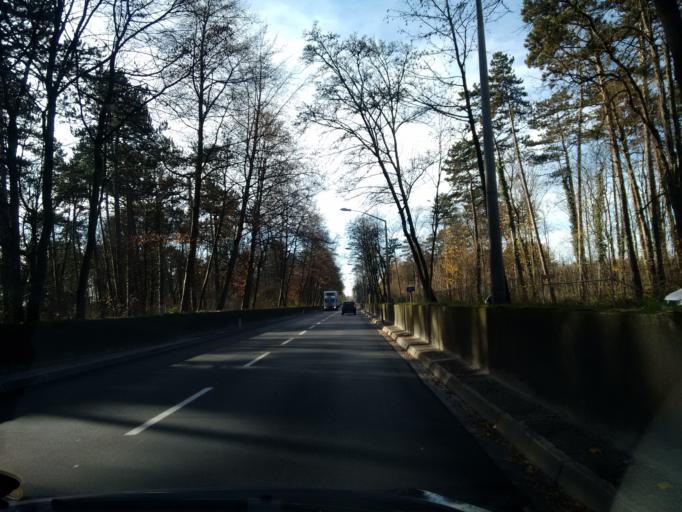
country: AT
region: Upper Austria
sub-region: Linz Stadt
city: Linz
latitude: 48.2670
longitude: 14.3076
